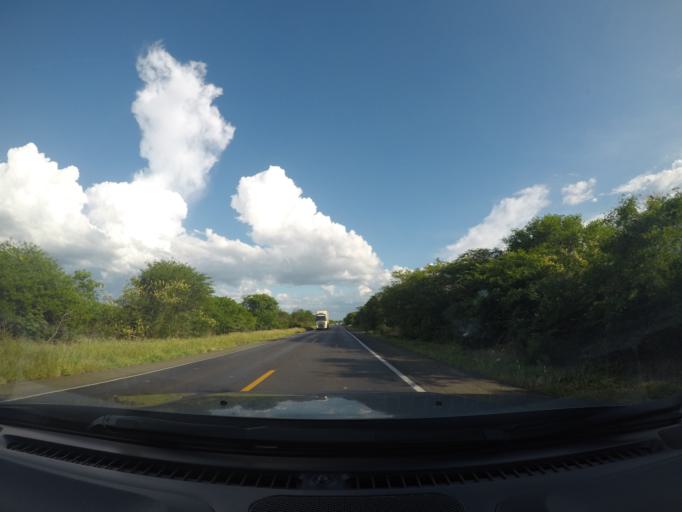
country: BR
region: Bahia
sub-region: Oliveira Dos Brejinhos
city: Oliveira dos Brejinhos
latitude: -12.0942
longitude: -42.9261
